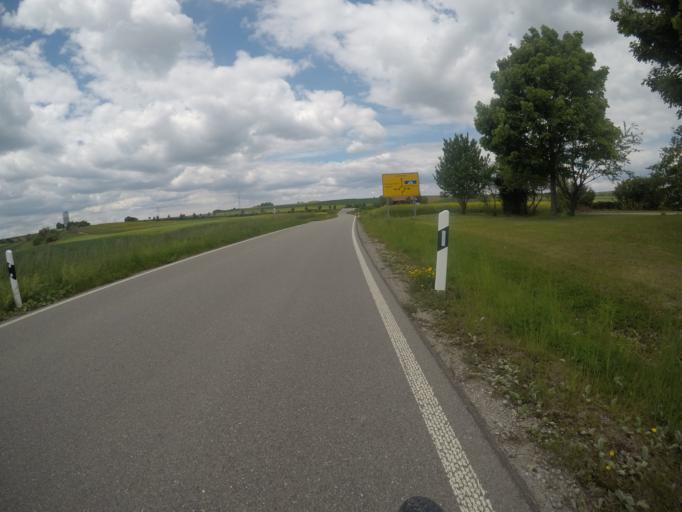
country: DE
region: Baden-Wuerttemberg
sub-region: Regierungsbezirk Stuttgart
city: Oberjettingen
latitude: 48.5781
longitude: 8.7647
